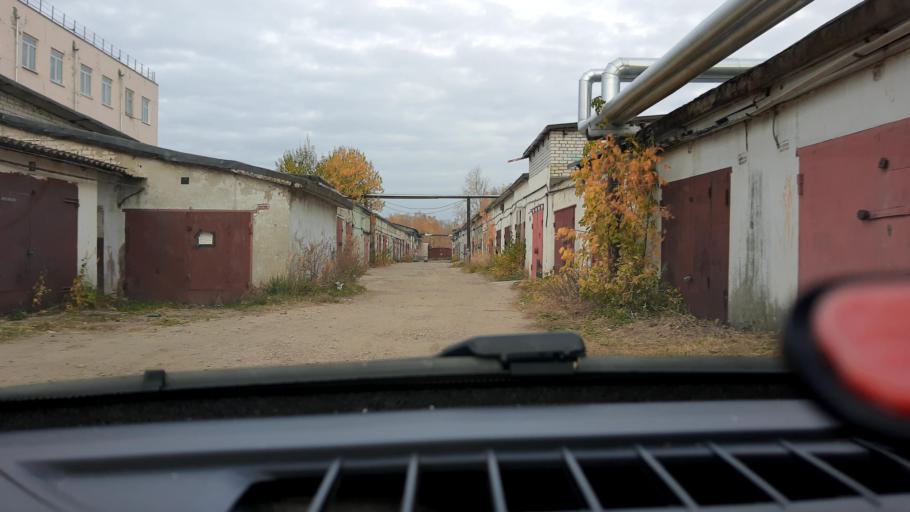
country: RU
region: Nizjnij Novgorod
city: Gorbatovka
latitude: 56.3271
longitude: 43.8472
